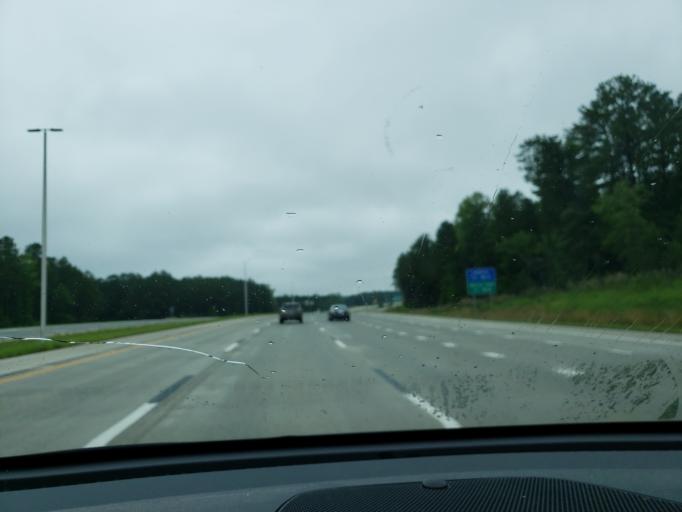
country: US
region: North Carolina
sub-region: Wake County
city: Apex
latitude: 35.6900
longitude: -78.8639
